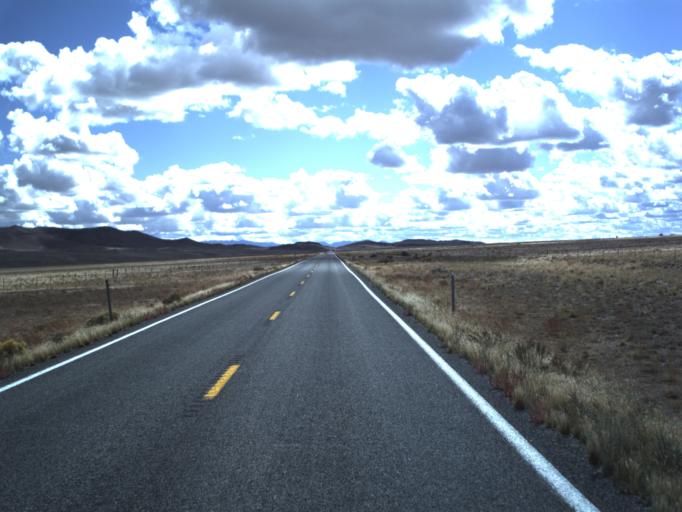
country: US
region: Utah
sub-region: Beaver County
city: Milford
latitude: 38.6732
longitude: -113.8866
